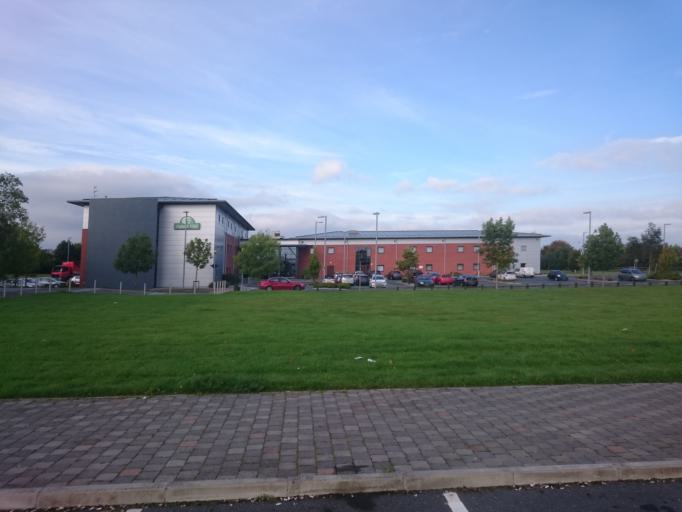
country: IE
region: Leinster
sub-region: Kilkenny
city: Kilkenny
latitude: 52.6348
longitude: -7.2475
